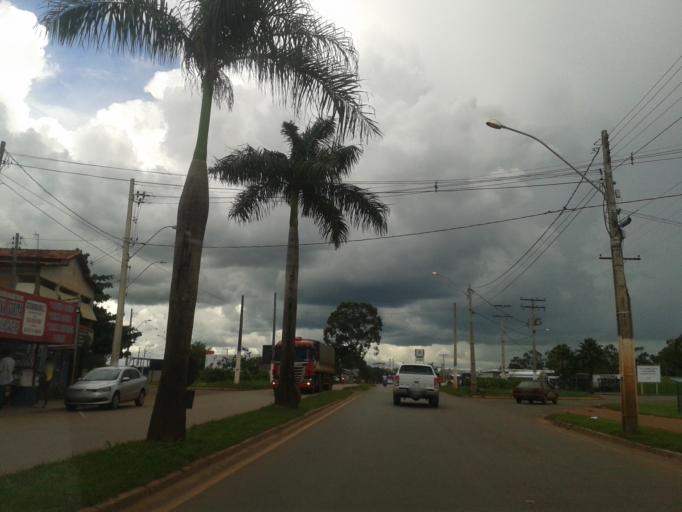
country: BR
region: Goias
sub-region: Itaberai
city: Itaberai
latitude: -16.0460
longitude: -49.7897
